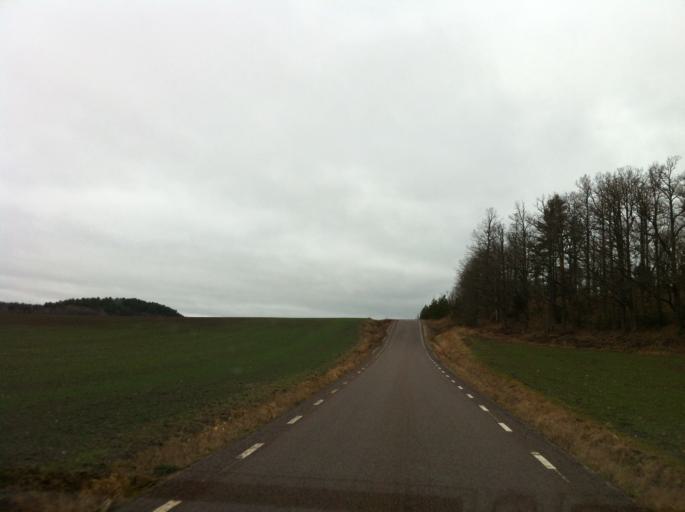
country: SE
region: Kalmar
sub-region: Vasterviks Kommun
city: Overum
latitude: 57.9025
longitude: 16.0840
